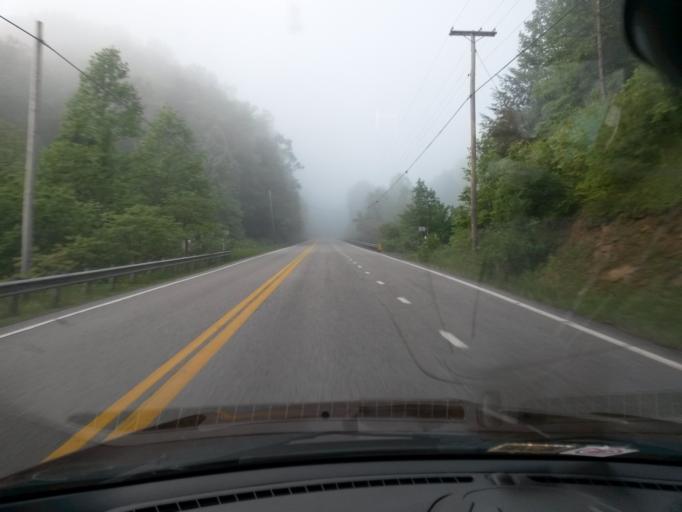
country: US
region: West Virginia
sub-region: McDowell County
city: Welch
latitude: 37.4968
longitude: -81.5390
